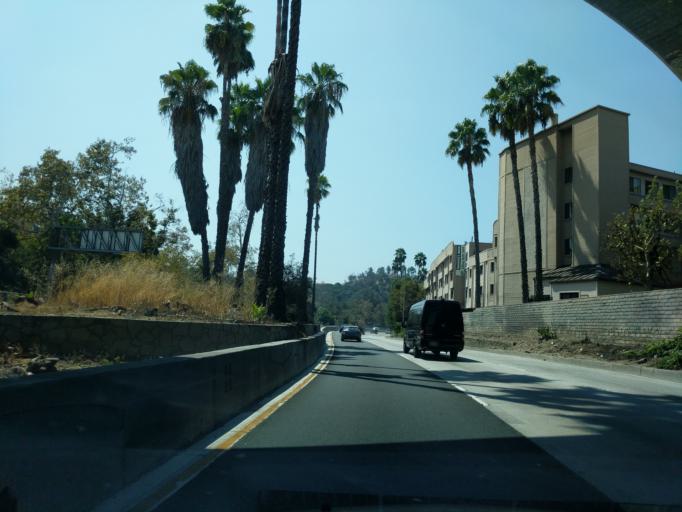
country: US
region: California
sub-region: Los Angeles County
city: South Pasadena
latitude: 34.1129
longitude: -118.1773
